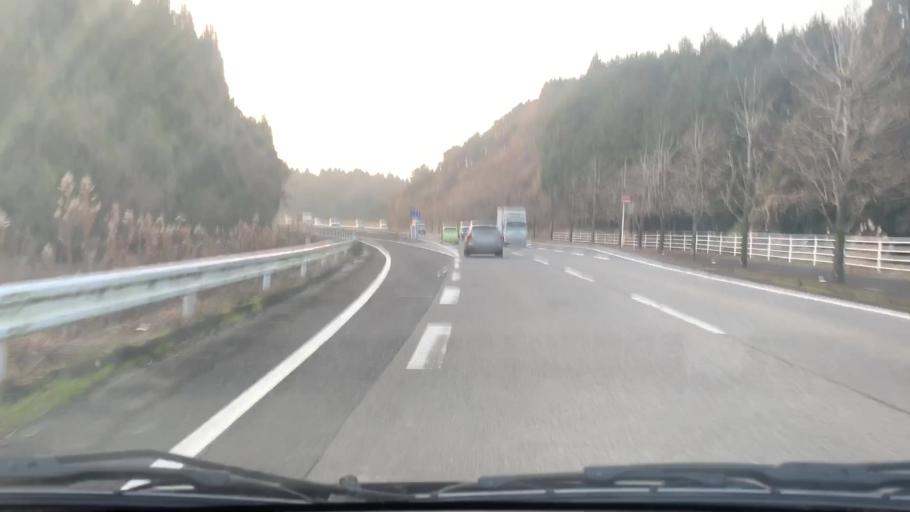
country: JP
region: Saga Prefecture
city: Imaricho-ko
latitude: 33.2660
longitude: 129.9554
